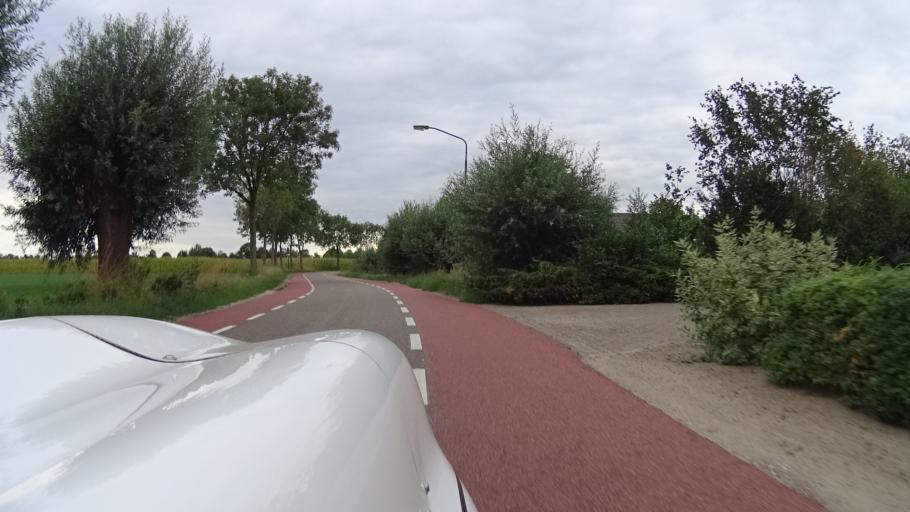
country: NL
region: North Brabant
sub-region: Gemeente Bernheze
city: Loosbroek
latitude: 51.6843
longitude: 5.4992
